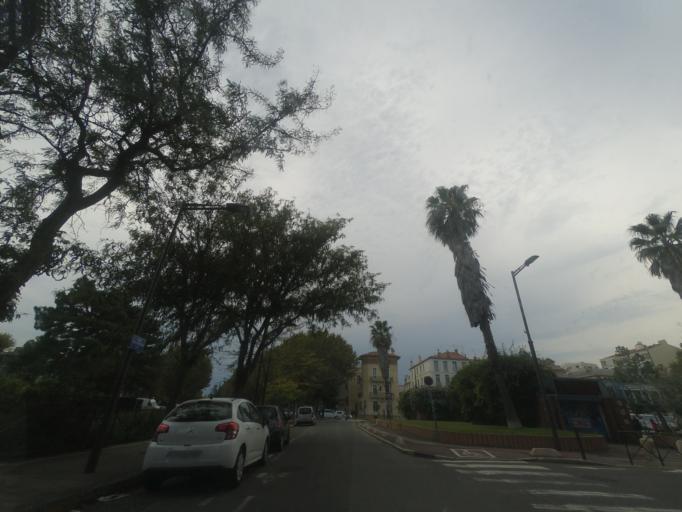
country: FR
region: Languedoc-Roussillon
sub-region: Departement des Pyrenees-Orientales
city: Perpignan
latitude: 42.6975
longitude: 2.8888
